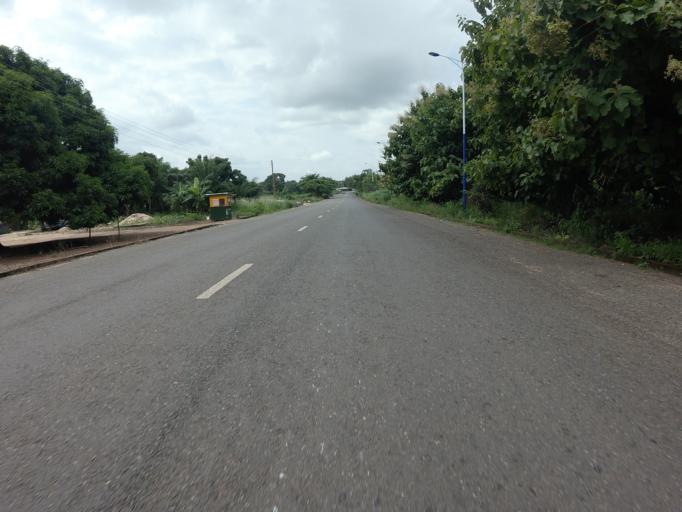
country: GH
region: Volta
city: Ho
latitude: 6.6185
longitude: 0.4942
